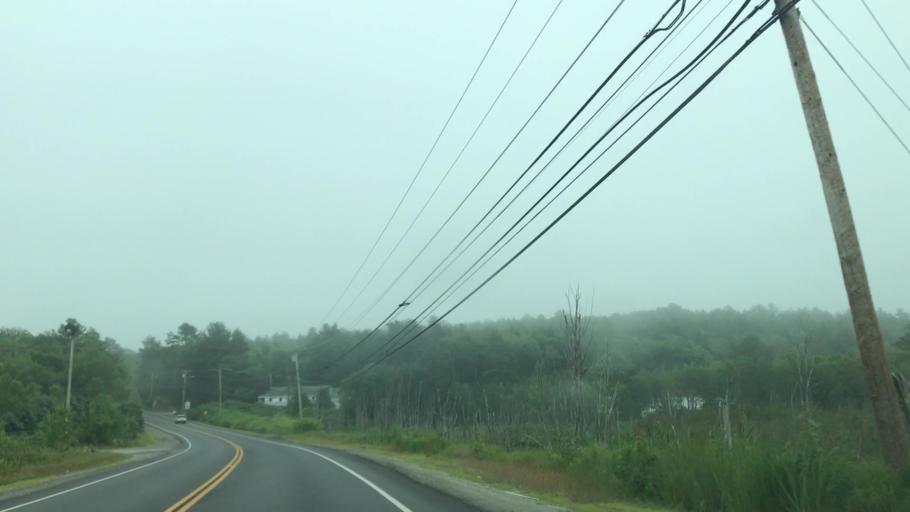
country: US
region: Maine
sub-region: Sagadahoc County
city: Bath
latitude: 43.9053
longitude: -69.8604
